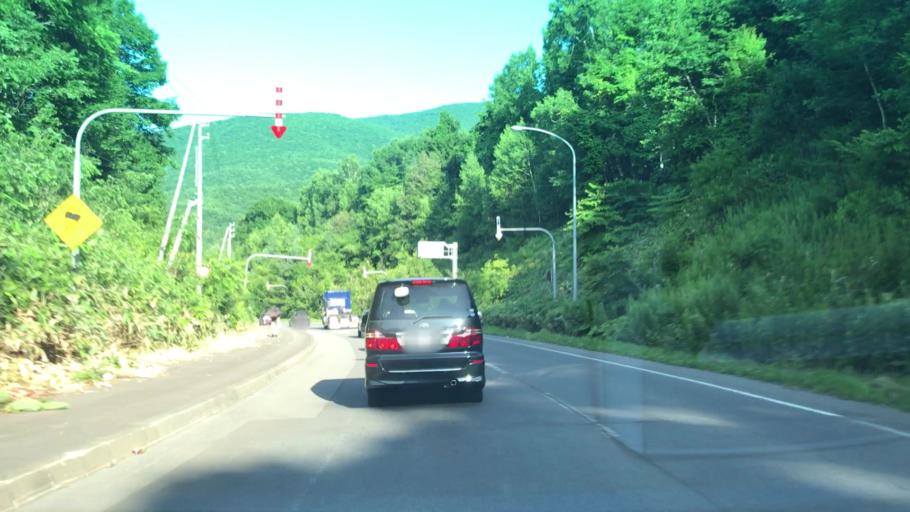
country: JP
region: Hokkaido
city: Otaru
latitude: 43.1590
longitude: 141.0380
